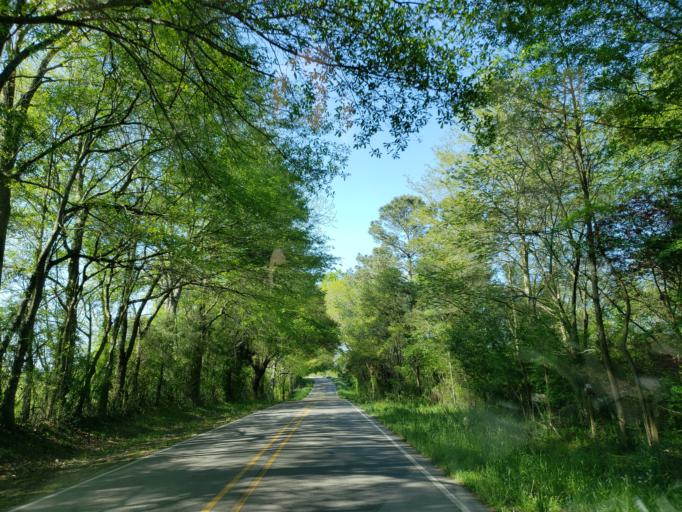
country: US
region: Mississippi
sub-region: Jones County
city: Ellisville
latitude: 31.5668
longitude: -89.3689
